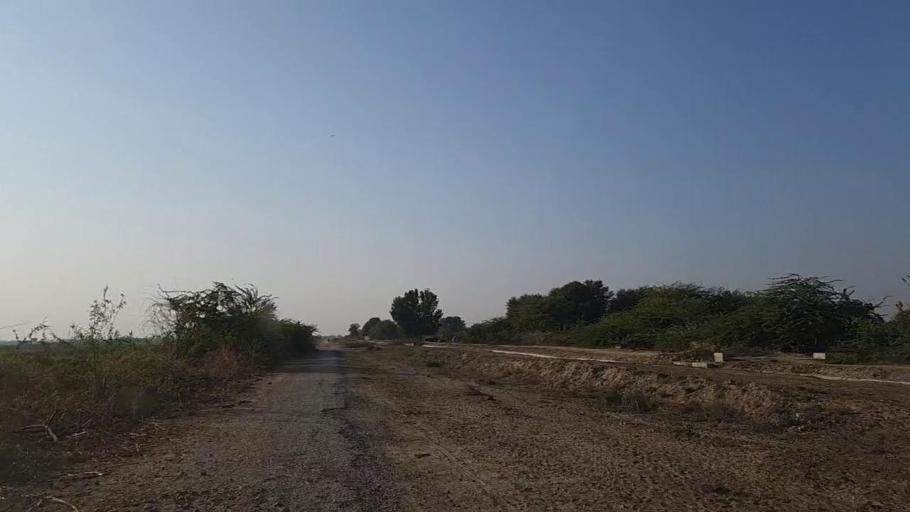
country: PK
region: Sindh
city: Naukot
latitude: 24.9134
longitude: 69.4523
